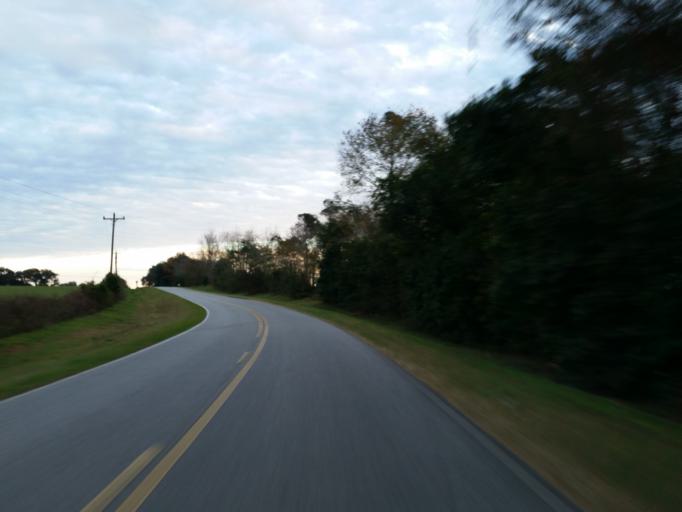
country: US
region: Florida
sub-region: Hamilton County
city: Jasper
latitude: 30.5230
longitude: -83.0891
